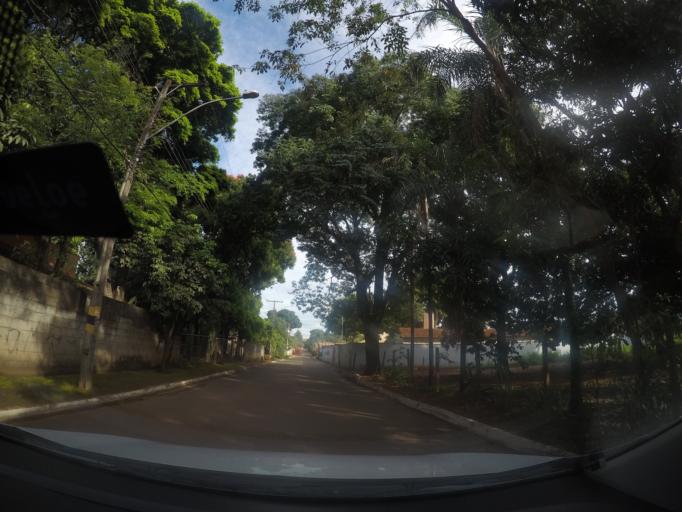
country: BR
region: Goias
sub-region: Goiania
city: Goiania
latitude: -16.6361
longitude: -49.3501
